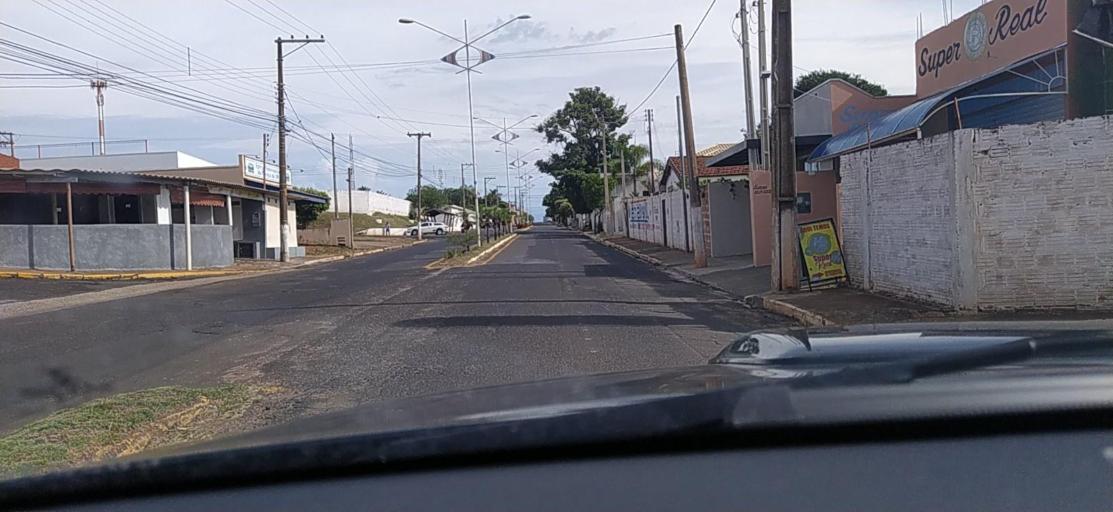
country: BR
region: Sao Paulo
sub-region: Catanduva
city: Catanduva
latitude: -21.0621
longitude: -49.0627
